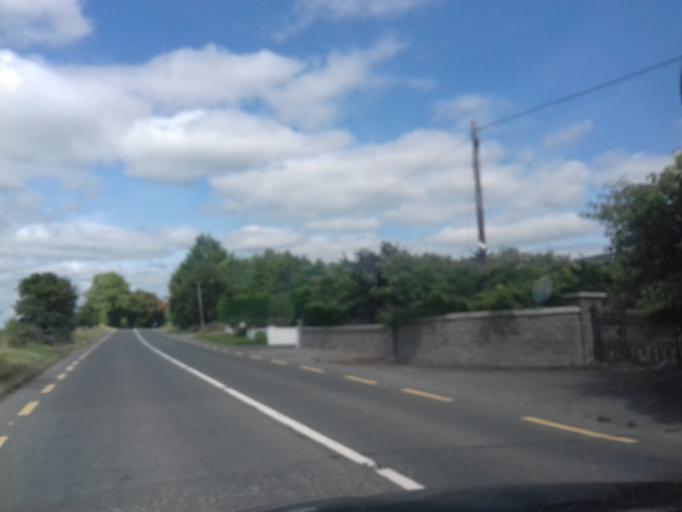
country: IE
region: Leinster
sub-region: Wicklow
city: Valleymount
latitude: 53.0475
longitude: -6.6332
